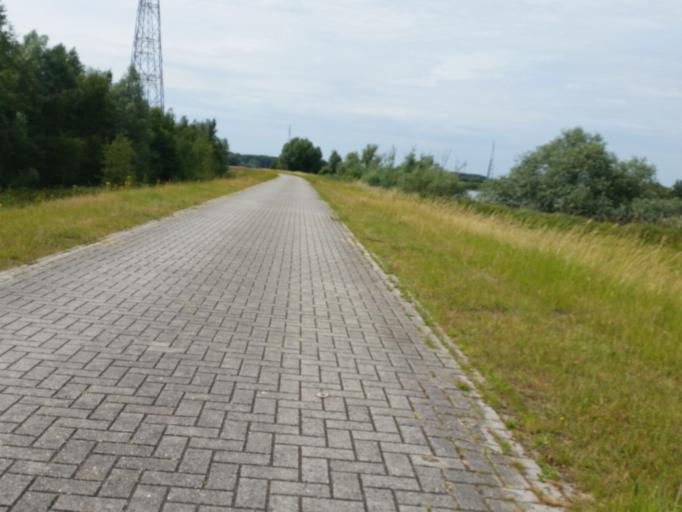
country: BE
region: Flanders
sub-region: Provincie Antwerpen
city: Niel
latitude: 51.1031
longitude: 4.3125
